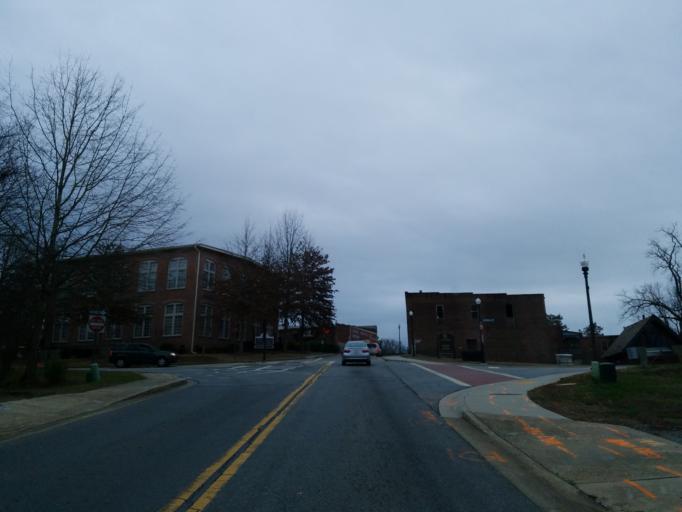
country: US
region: Georgia
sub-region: Cobb County
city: Acworth
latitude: 34.0675
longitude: -84.6771
